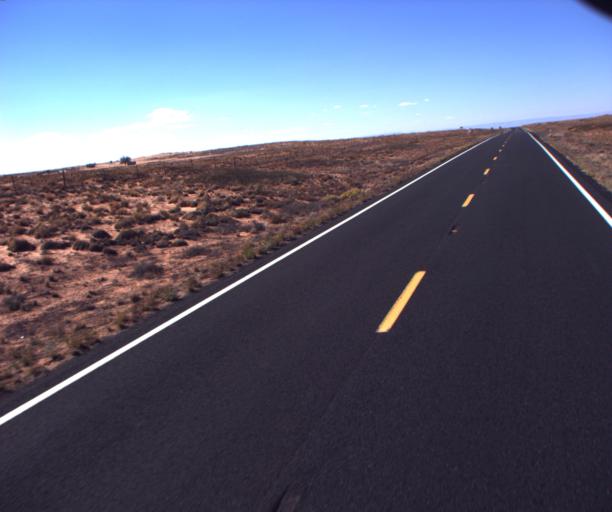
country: US
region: Arizona
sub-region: Coconino County
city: Tuba City
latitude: 36.0186
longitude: -111.1104
